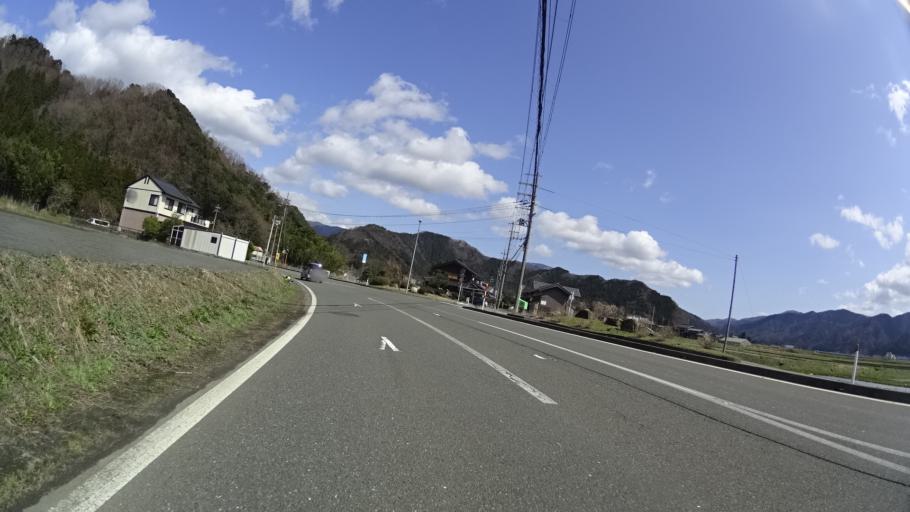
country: JP
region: Fukui
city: Obama
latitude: 35.4687
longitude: 135.8623
